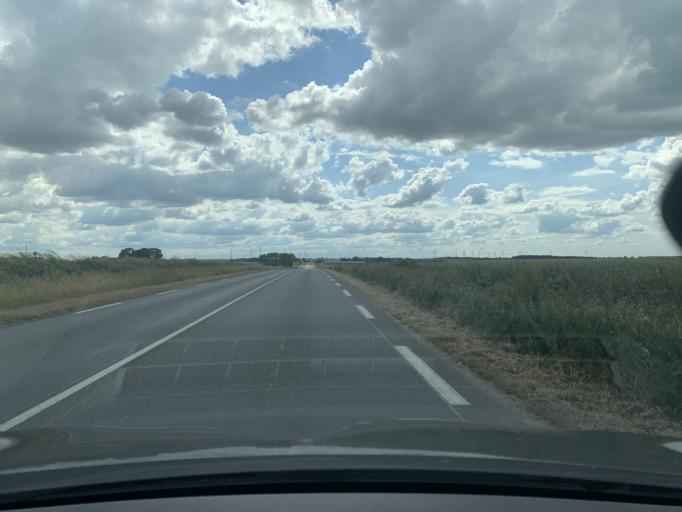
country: FR
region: Nord-Pas-de-Calais
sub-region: Departement du Nord
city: Gouzeaucourt
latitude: 50.0658
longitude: 3.1555
